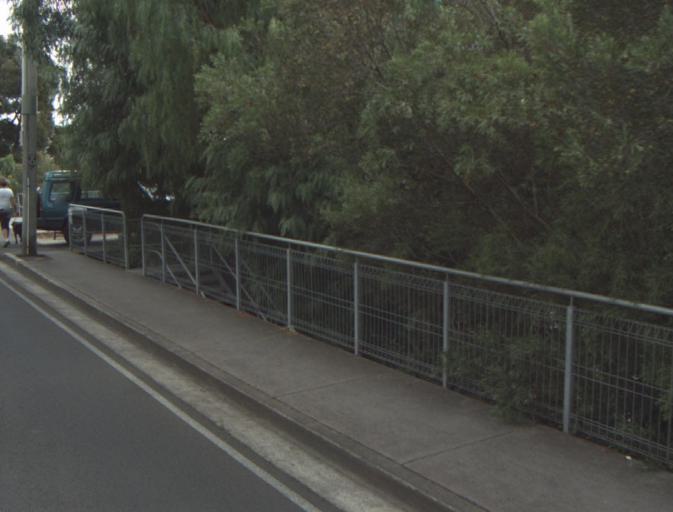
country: AU
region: Tasmania
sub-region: Launceston
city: Launceston
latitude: -41.4362
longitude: 147.1235
